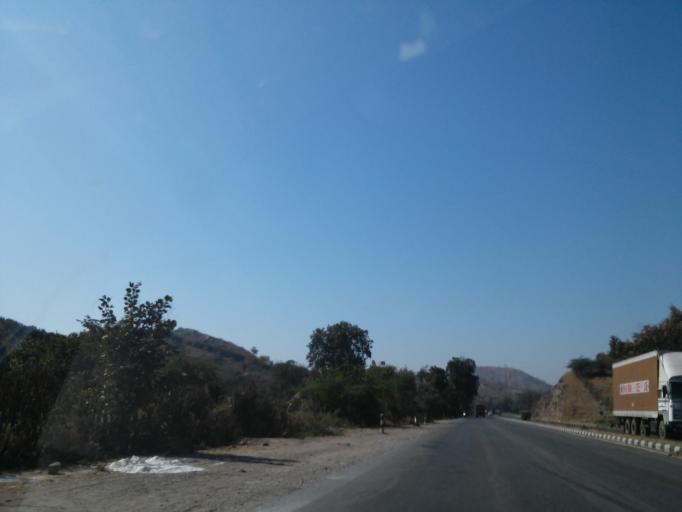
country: IN
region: Rajasthan
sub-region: Dungarpur
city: Dungarpur
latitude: 24.1330
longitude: 73.6949
